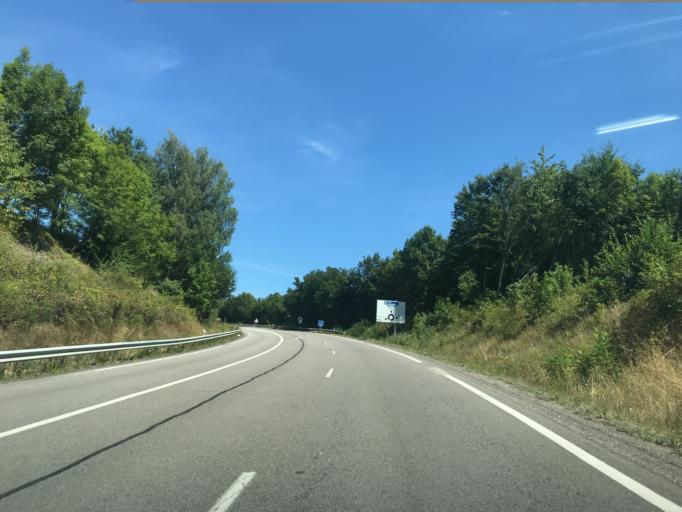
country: FR
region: Limousin
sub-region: Departement de la Correze
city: Tulle
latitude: 45.2808
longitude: 1.7961
